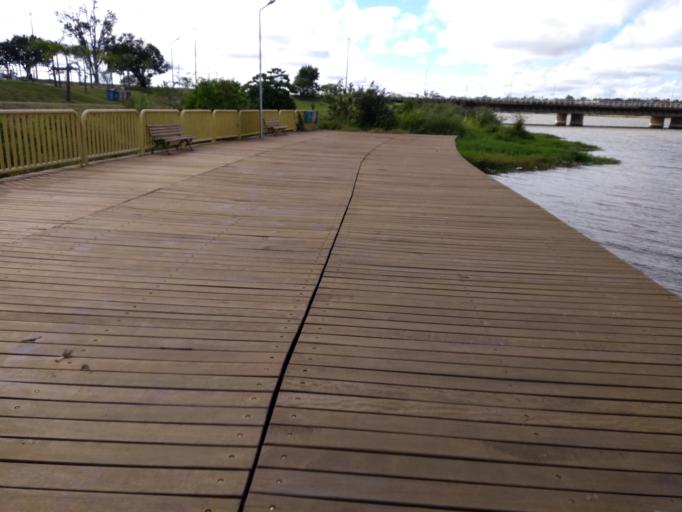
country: BR
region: Federal District
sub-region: Brasilia
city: Brasilia
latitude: -15.8385
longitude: -47.9002
